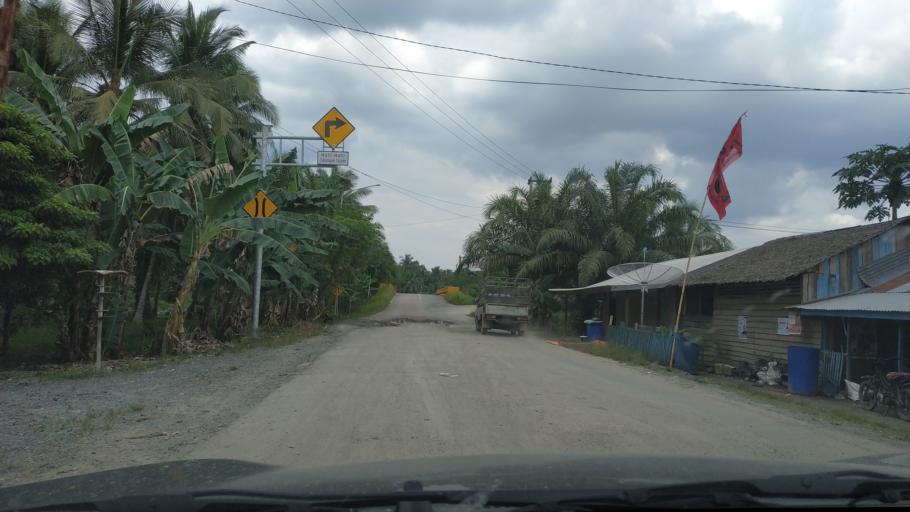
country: ID
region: Riau
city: Sungaisalak
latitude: -0.5638
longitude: 102.9641
